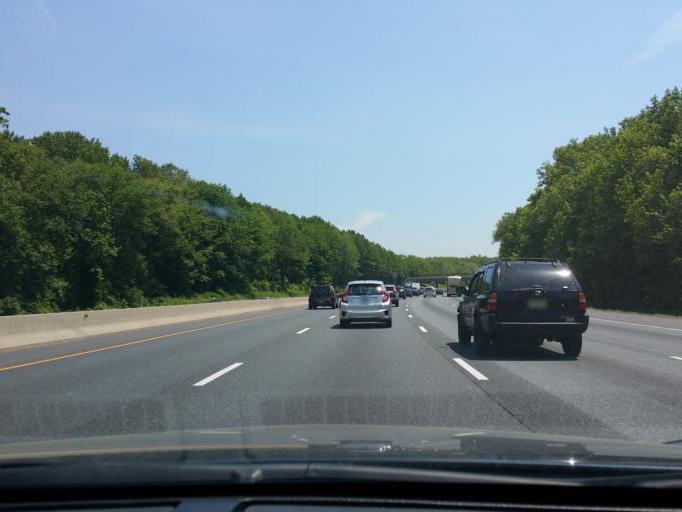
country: US
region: Maryland
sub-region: Harford County
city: Joppatowne
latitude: 39.4411
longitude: -76.3693
